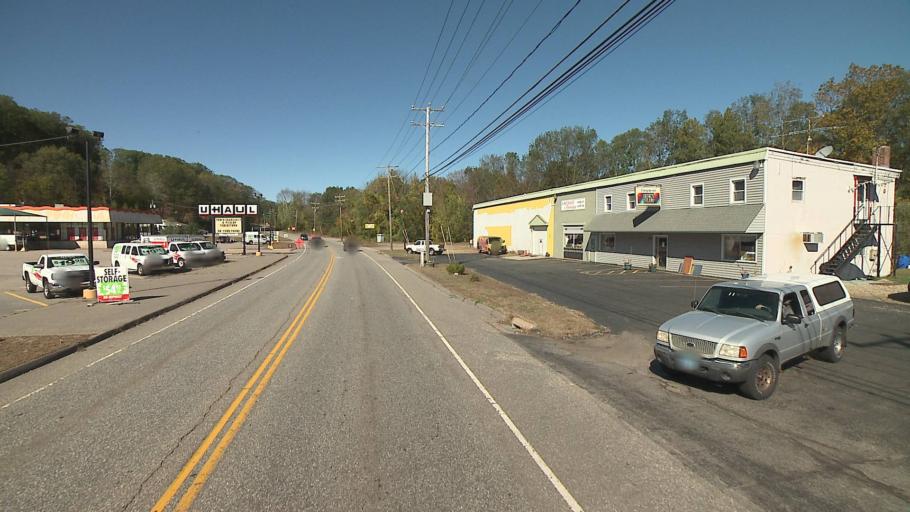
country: US
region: Connecticut
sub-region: Windham County
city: Willimantic
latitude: 41.7188
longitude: -72.2485
